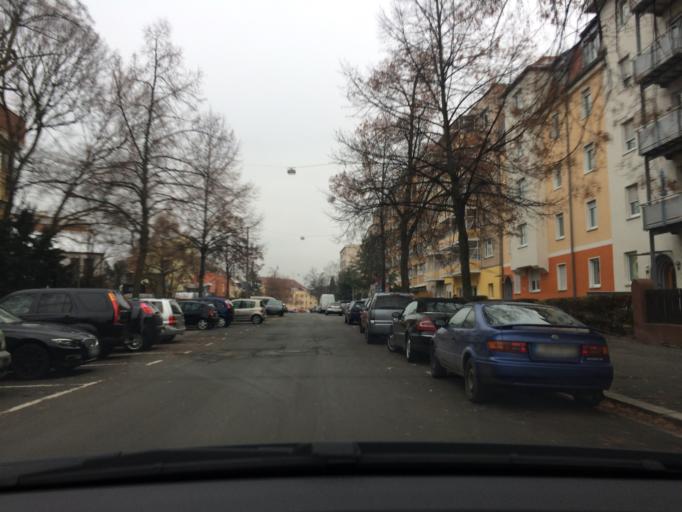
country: DE
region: Bavaria
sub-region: Regierungsbezirk Mittelfranken
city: Nuernberg
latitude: 49.4359
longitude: 11.0886
